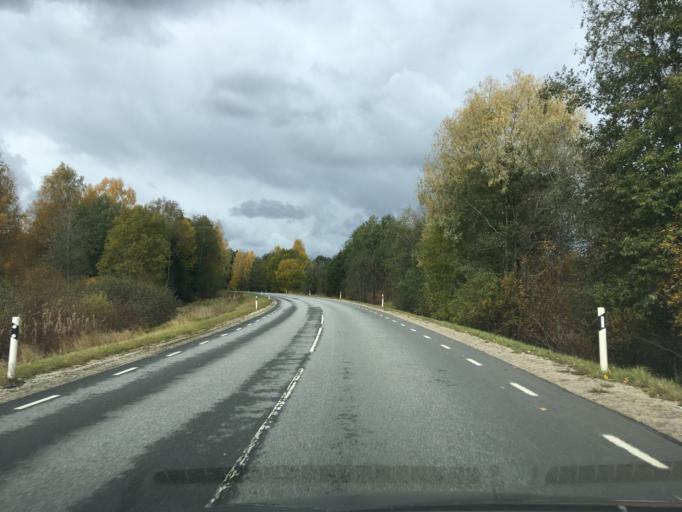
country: EE
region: Harju
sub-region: Anija vald
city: Kehra
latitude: 59.2937
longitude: 25.3747
